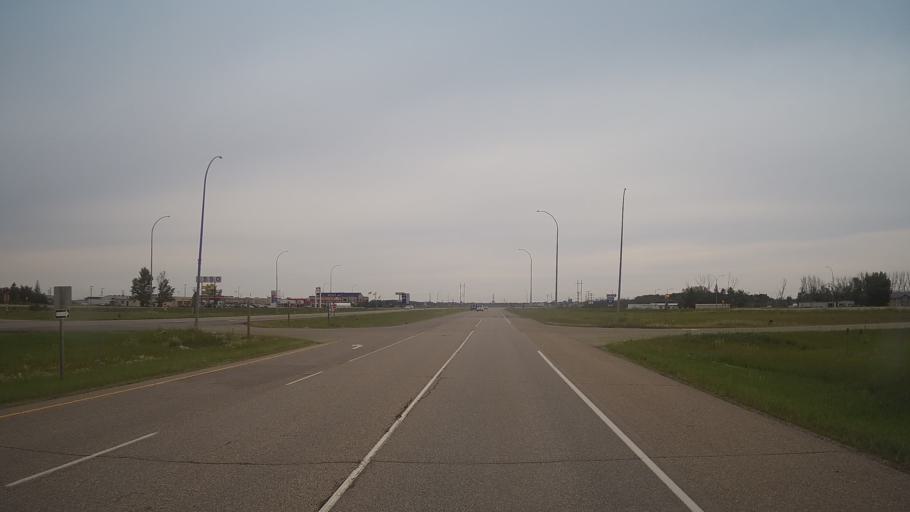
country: CA
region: Saskatchewan
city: Saskatoon
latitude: 52.0533
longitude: -106.5970
